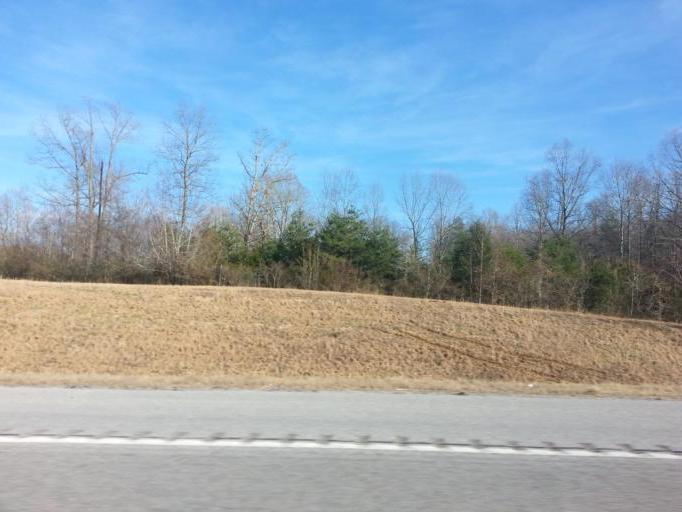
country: US
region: Tennessee
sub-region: Van Buren County
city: Spencer
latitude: 35.7862
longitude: -85.5911
